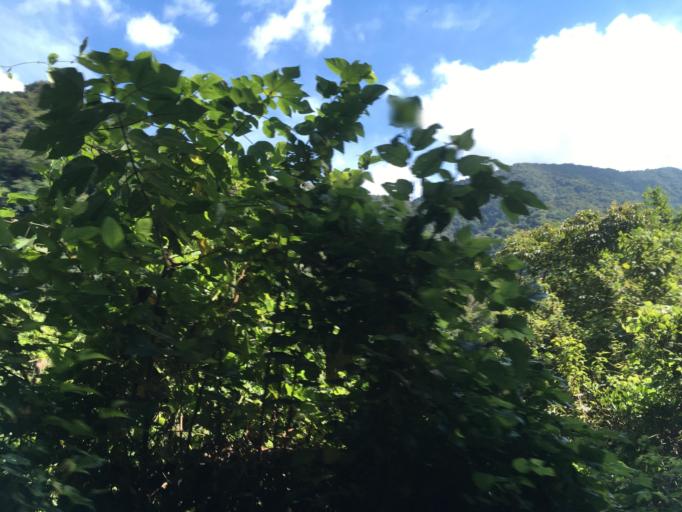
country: TW
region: Taiwan
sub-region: Yilan
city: Yilan
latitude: 24.4242
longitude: 121.7171
